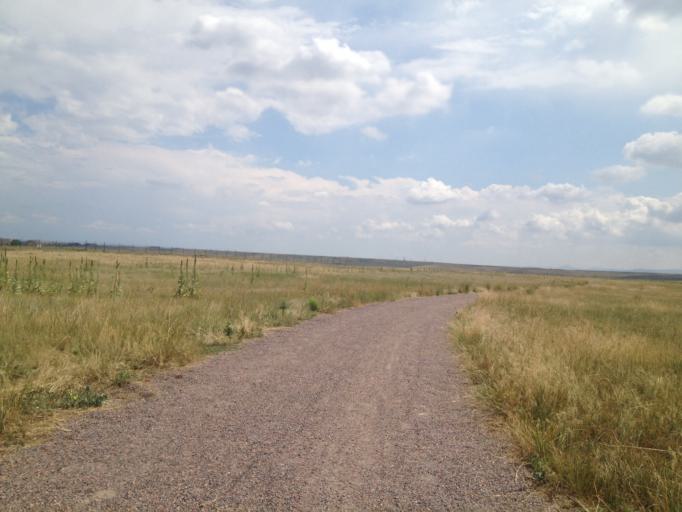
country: US
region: Colorado
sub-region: Boulder County
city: Superior
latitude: 39.9429
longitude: -105.1697
